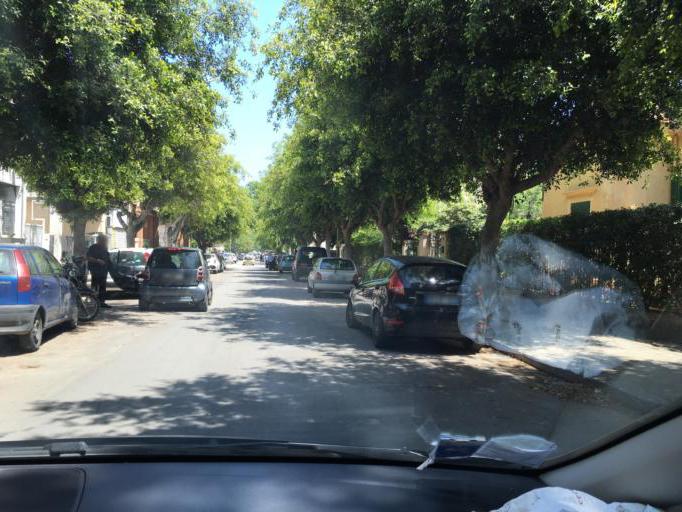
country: IT
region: Sicily
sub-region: Palermo
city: Palermo
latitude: 38.1978
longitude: 13.3174
